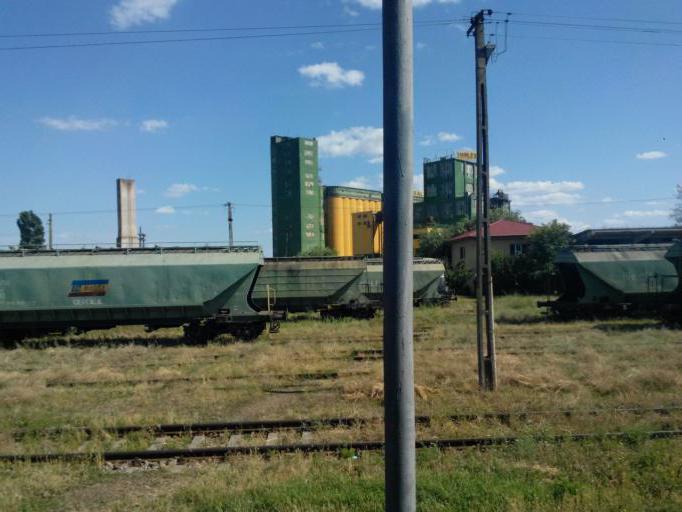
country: RO
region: Vaslui
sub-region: Municipiul Barlad
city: Barlad
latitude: 46.2146
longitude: 27.6724
